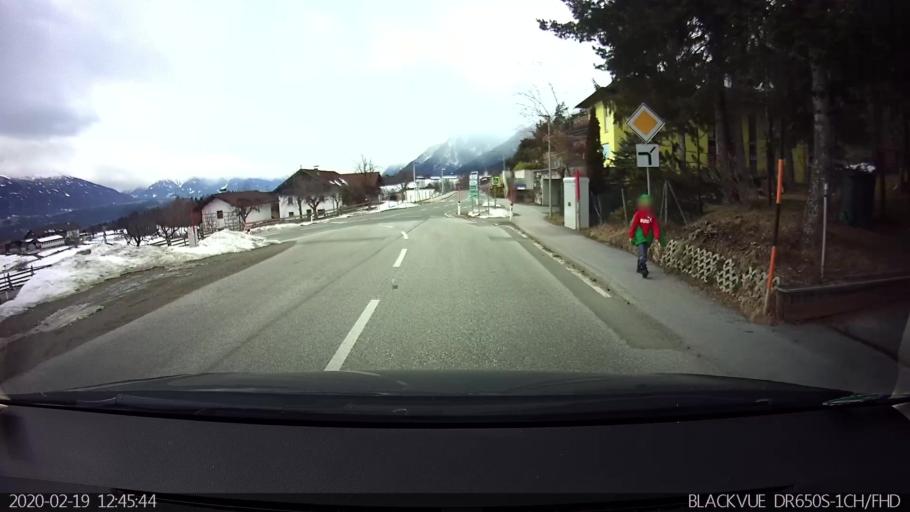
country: AT
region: Tyrol
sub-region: Politischer Bezirk Innsbruck Land
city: Gnadenwald
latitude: 47.3224
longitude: 11.5858
